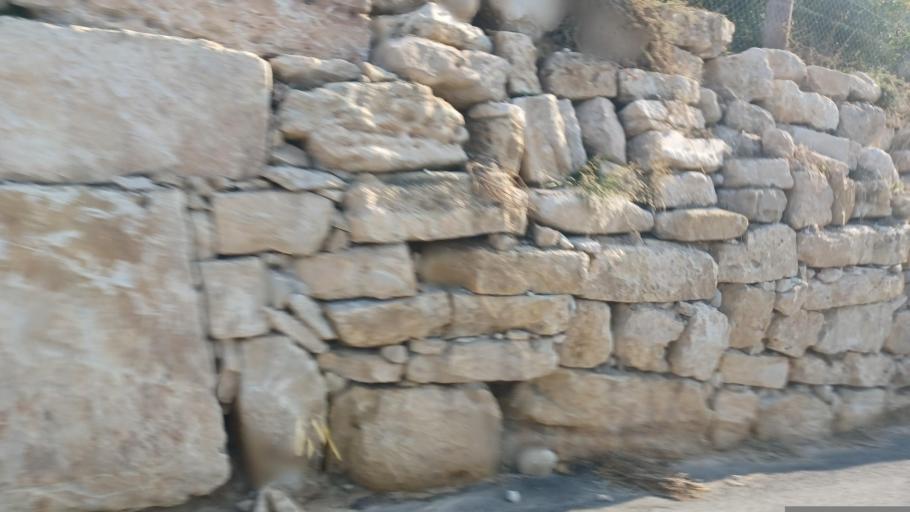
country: CY
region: Pafos
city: Pegeia
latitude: 34.9084
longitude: 32.3346
